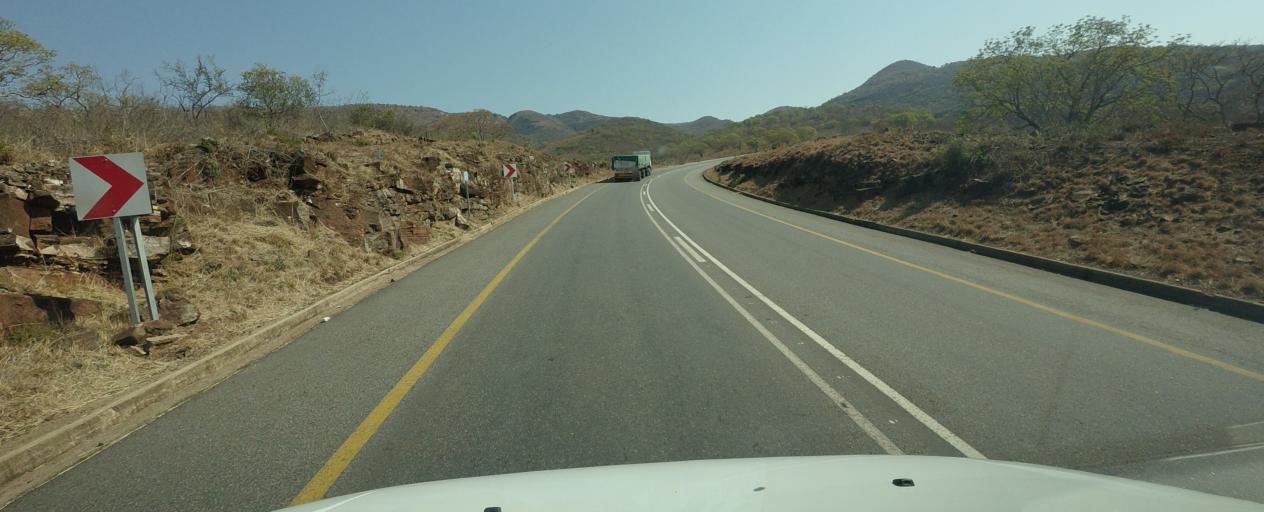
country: ZA
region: Mpumalanga
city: Burgersfort
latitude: -24.5547
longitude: 30.6206
